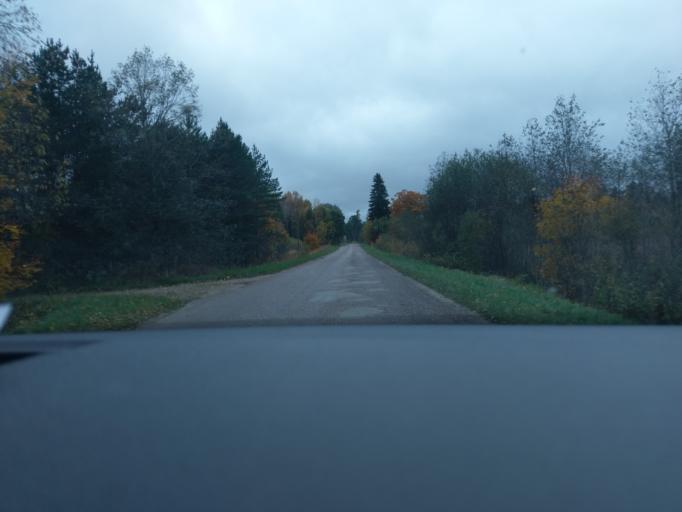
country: LV
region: Talsu Rajons
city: Stende
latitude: 57.0809
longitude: 22.2785
